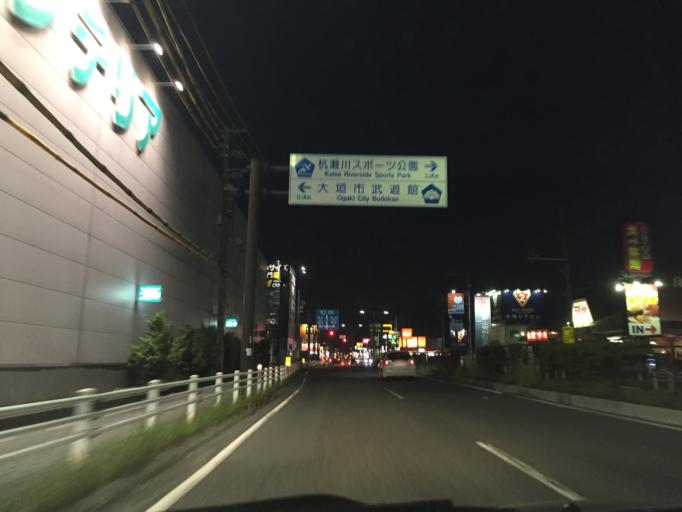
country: JP
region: Gifu
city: Ogaki
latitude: 35.3374
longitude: 136.6215
